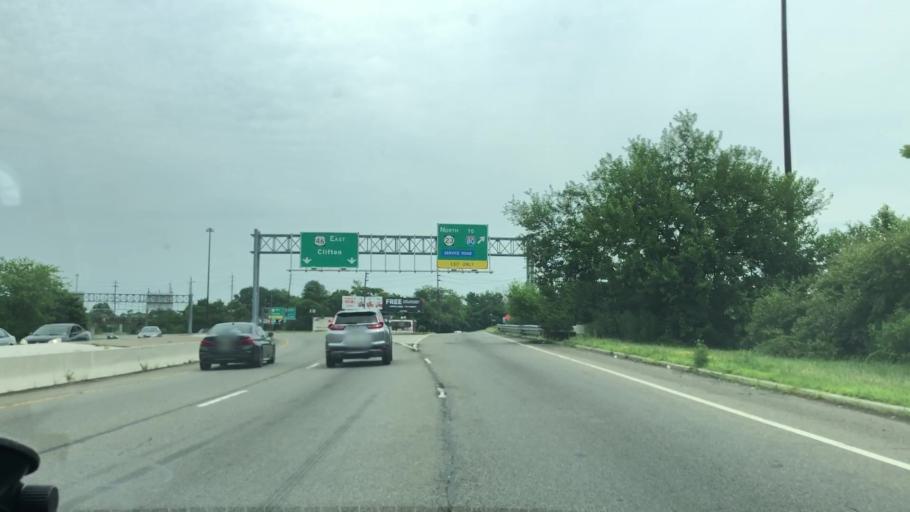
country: US
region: New Jersey
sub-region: Passaic County
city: Singac
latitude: 40.8930
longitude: -74.2554
